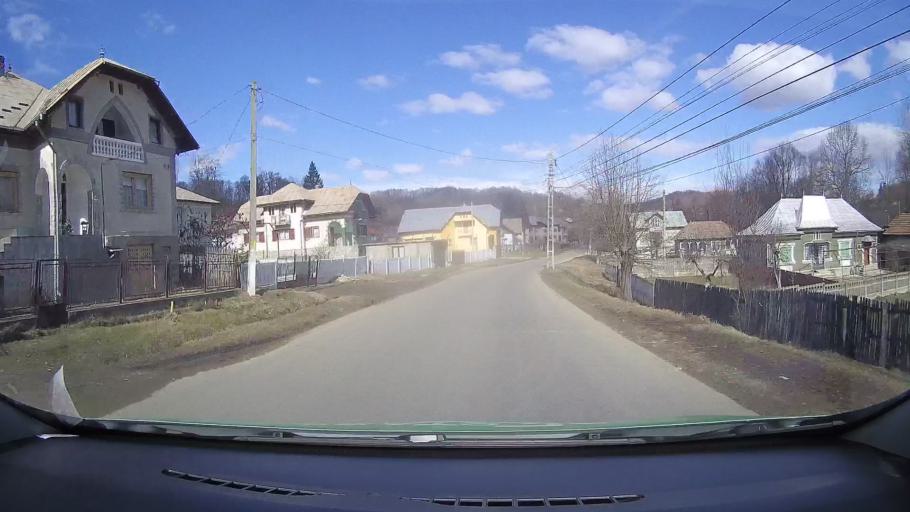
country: RO
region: Dambovita
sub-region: Comuna Vulcana Bai
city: Vulcana Bai
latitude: 45.0702
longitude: 25.3784
